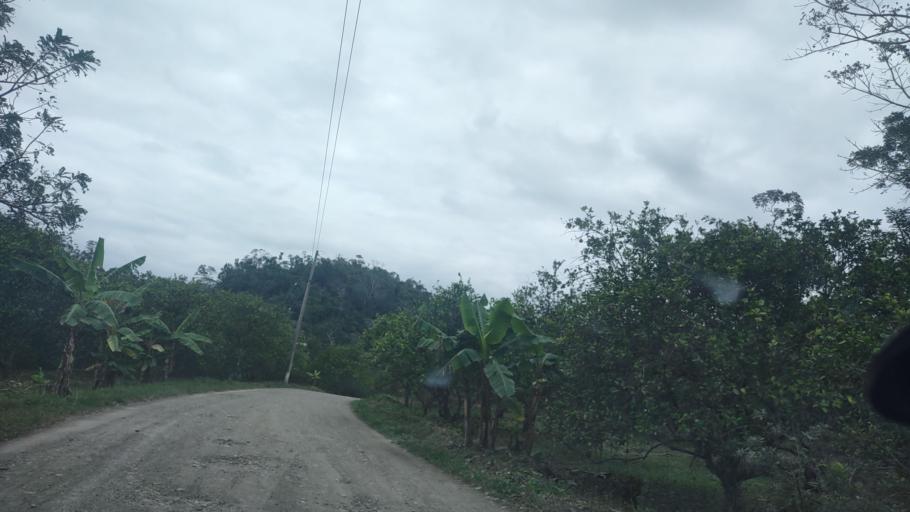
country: MX
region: Veracruz
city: Papantla de Olarte
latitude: 20.4317
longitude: -97.2646
